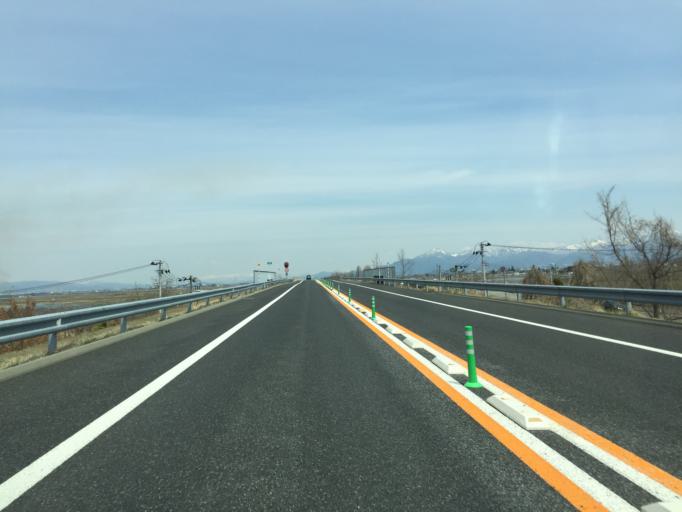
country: JP
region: Yamagata
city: Tendo
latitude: 38.3249
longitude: 140.3267
